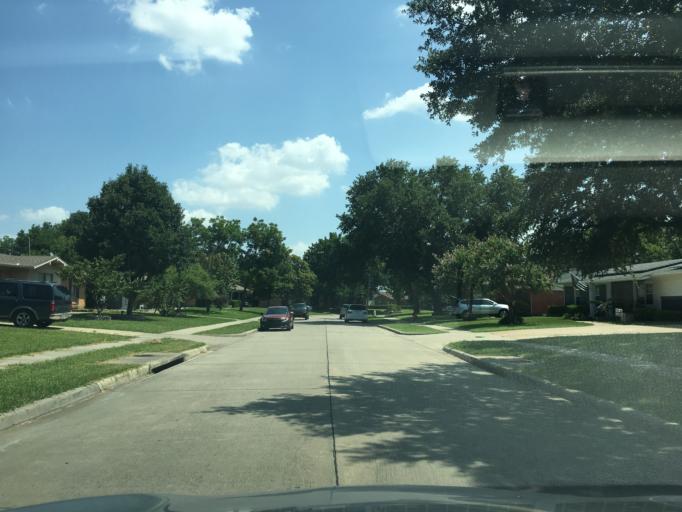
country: US
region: Texas
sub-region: Dallas County
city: Farmers Branch
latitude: 32.9193
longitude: -96.8611
